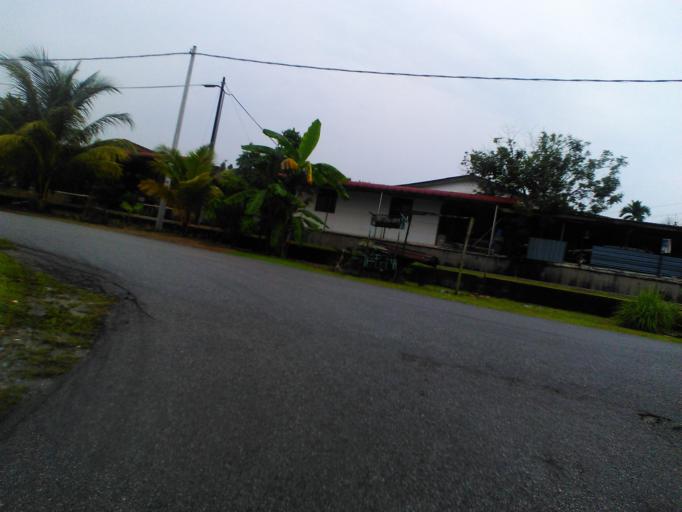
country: MY
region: Kedah
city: Kulim
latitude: 5.3620
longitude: 100.5777
